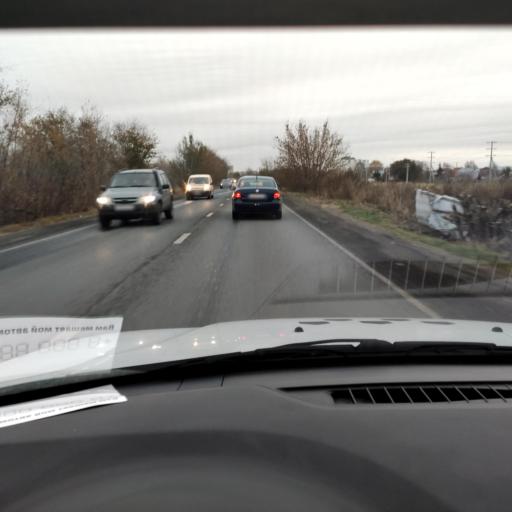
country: RU
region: Samara
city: Podstepki
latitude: 53.5164
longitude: 49.2346
